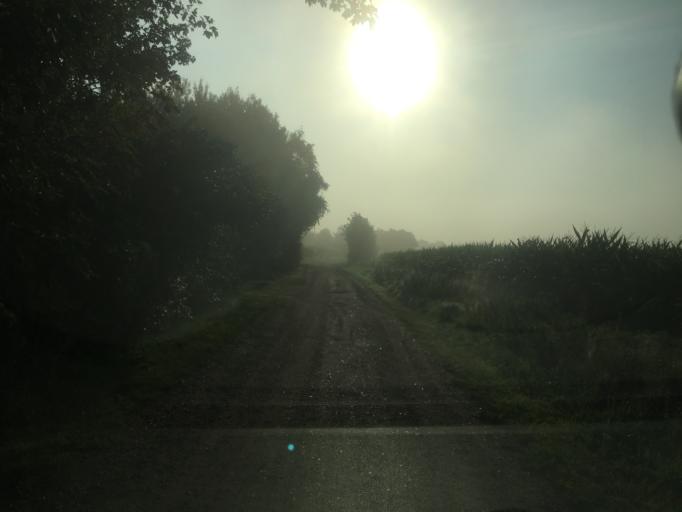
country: DK
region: South Denmark
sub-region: Tonder Kommune
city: Logumkloster
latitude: 55.0135
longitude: 8.9095
